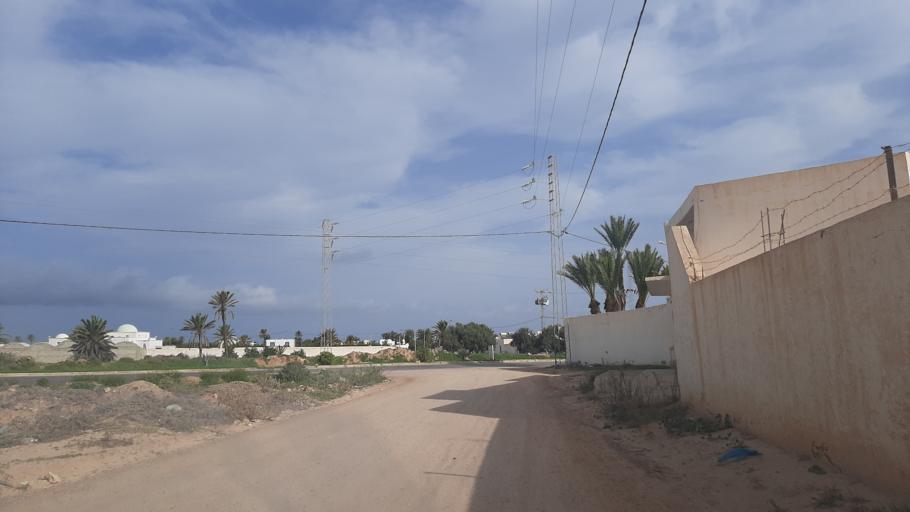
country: TN
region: Madanin
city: Midoun
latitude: 33.8176
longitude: 11.0260
